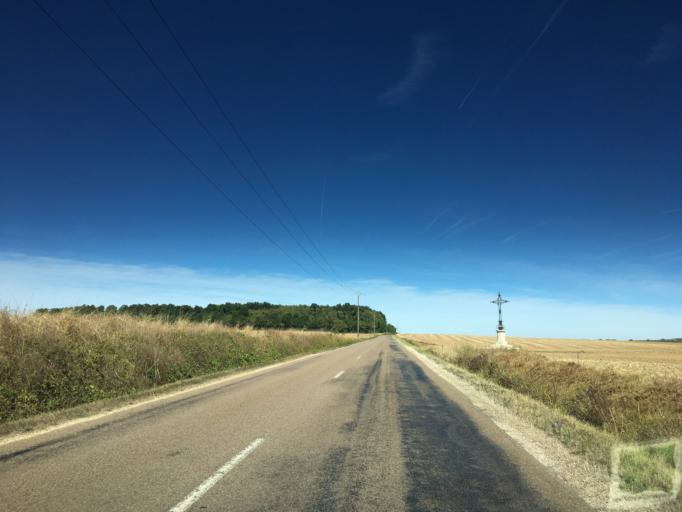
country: FR
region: Bourgogne
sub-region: Departement de l'Yonne
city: Saint-Bris-le-Vineux
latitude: 47.6712
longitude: 3.6592
